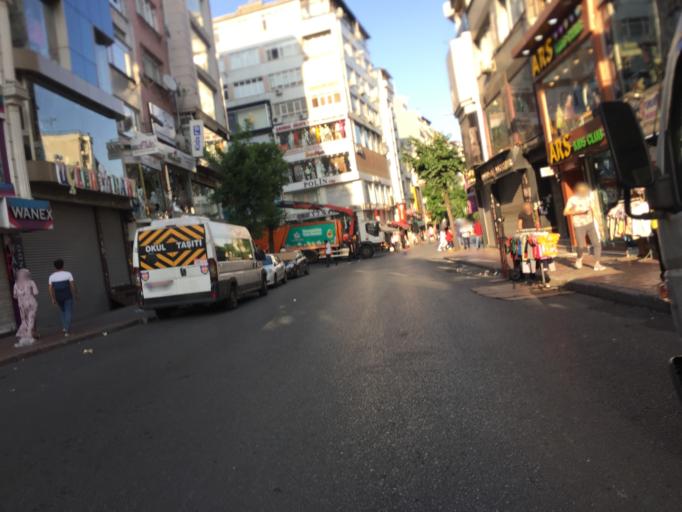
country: TR
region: Istanbul
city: Istanbul
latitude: 41.0071
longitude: 28.9574
